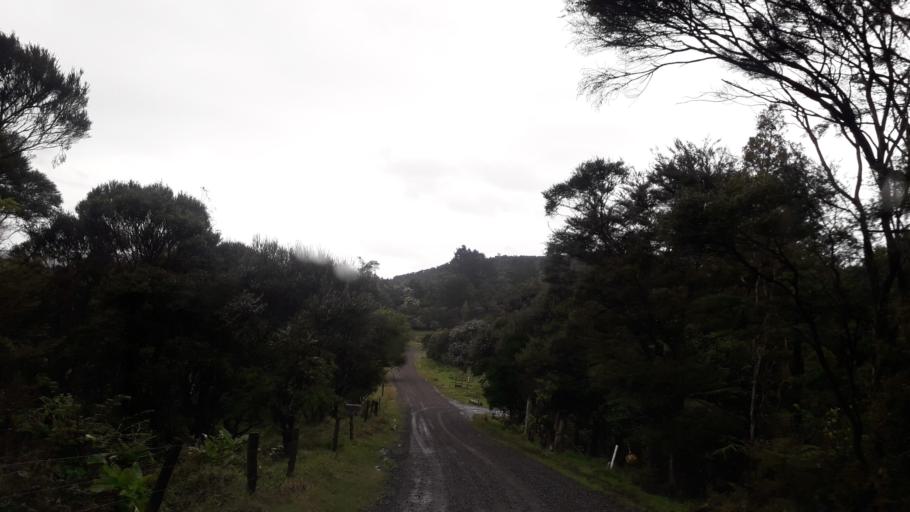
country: NZ
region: Northland
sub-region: Far North District
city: Kaitaia
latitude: -35.3917
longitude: 173.4036
